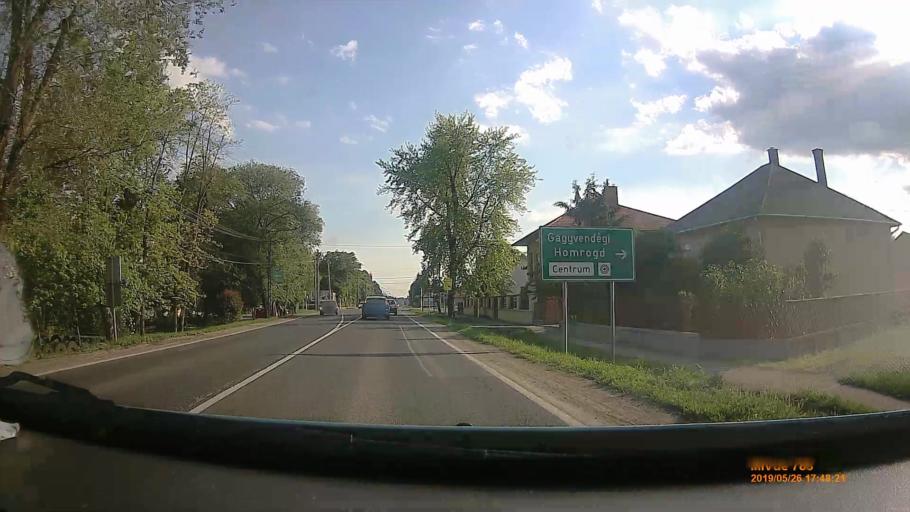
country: HU
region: Borsod-Abauj-Zemplen
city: Szikszo
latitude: 48.1959
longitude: 20.9301
